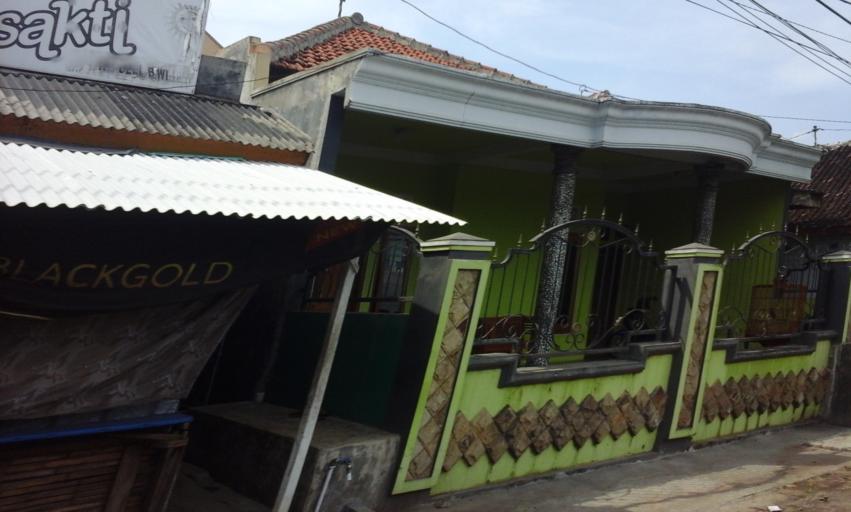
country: ID
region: East Java
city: Kertosari
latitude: -8.2794
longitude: 114.3170
